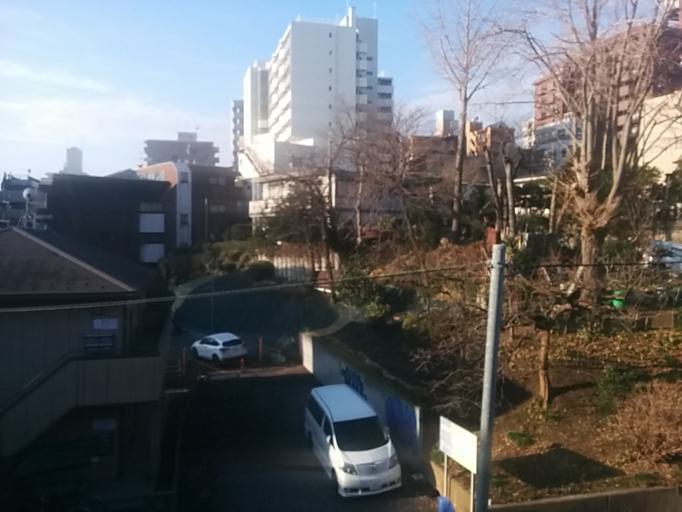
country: JP
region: Saitama
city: Wako
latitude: 35.7763
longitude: 139.6348
